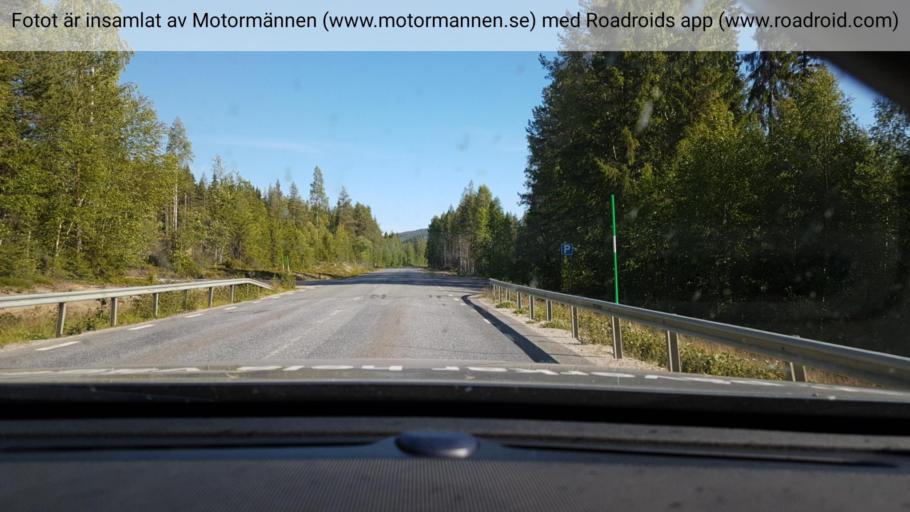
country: SE
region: Vaesterbotten
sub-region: Lycksele Kommun
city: Lycksele
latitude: 64.4509
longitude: 18.9336
